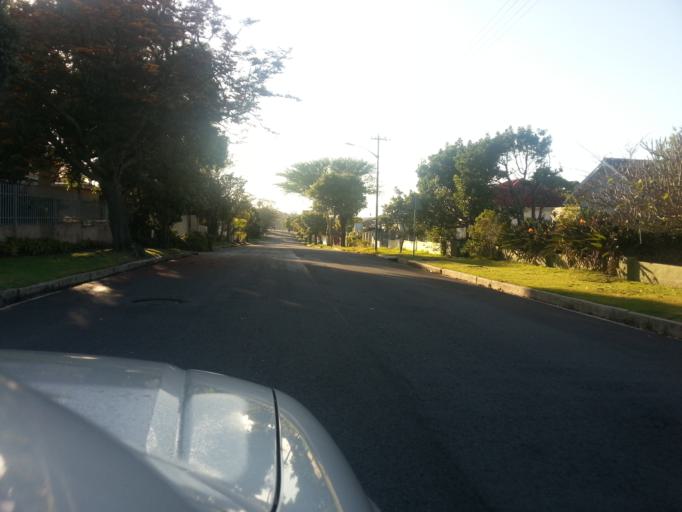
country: ZA
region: Eastern Cape
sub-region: Buffalo City Metropolitan Municipality
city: East London
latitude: -32.9861
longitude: 27.9257
